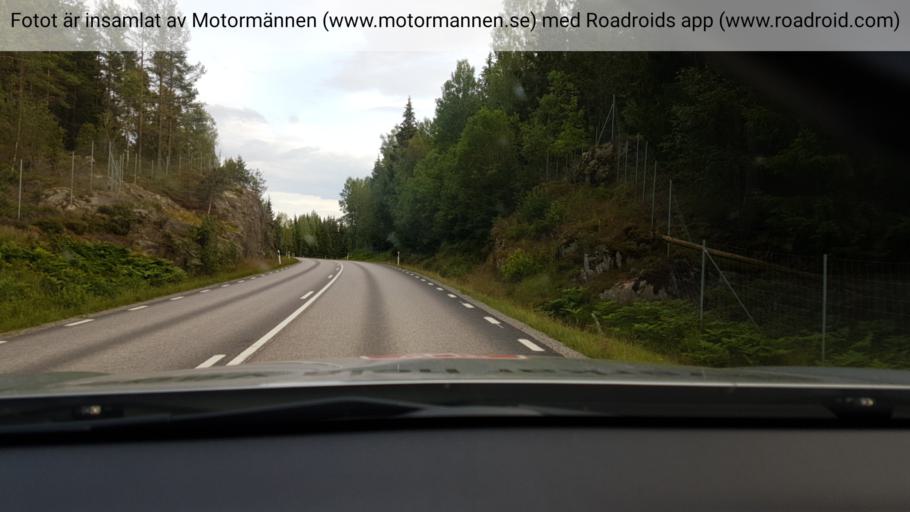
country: SE
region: Vaestra Goetaland
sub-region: Fargelanda Kommun
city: Faergelanda
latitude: 58.4702
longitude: 12.0176
